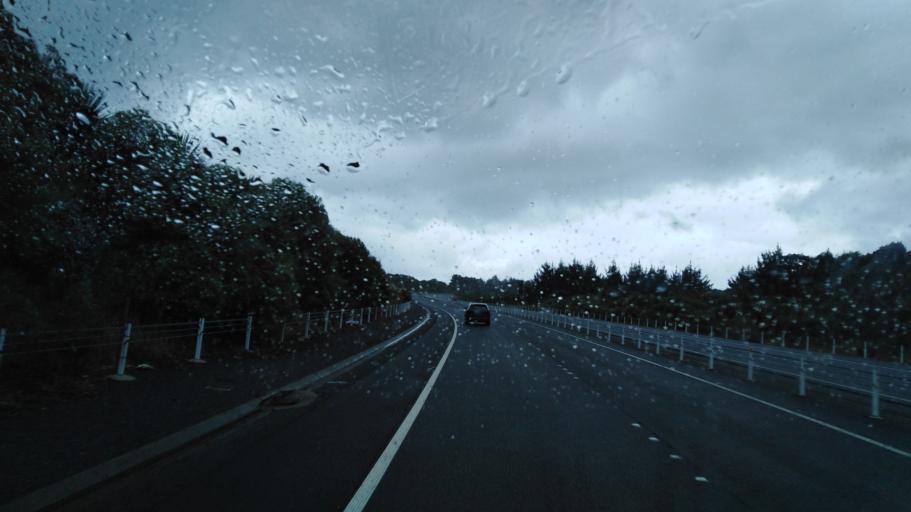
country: NZ
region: Wellington
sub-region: Kapiti Coast District
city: Paraparaumu
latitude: -40.9327
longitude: 174.9942
